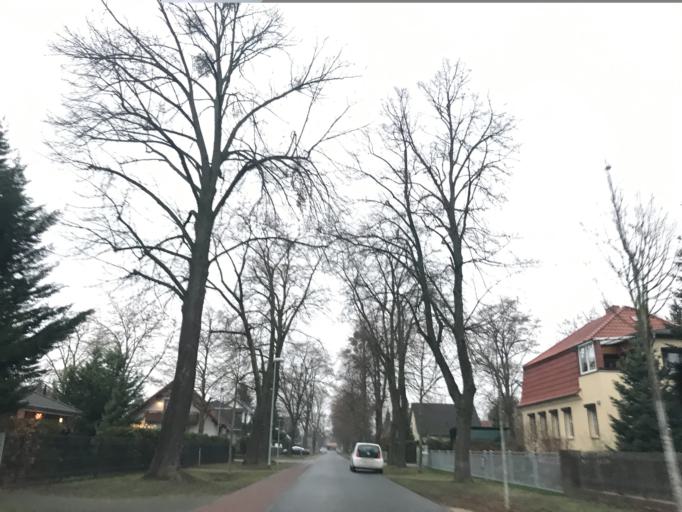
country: DE
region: Brandenburg
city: Falkensee
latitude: 52.5559
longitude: 13.1167
